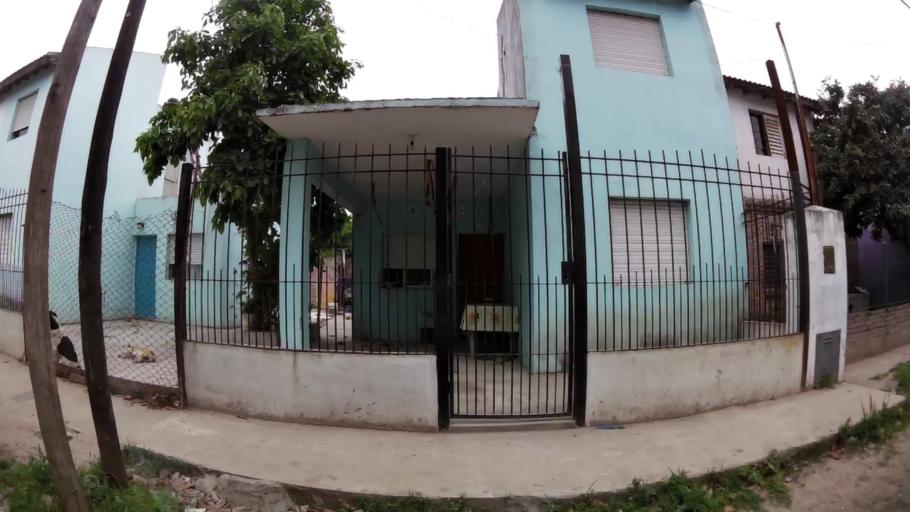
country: AR
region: Buenos Aires
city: San Justo
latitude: -34.6975
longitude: -58.5508
